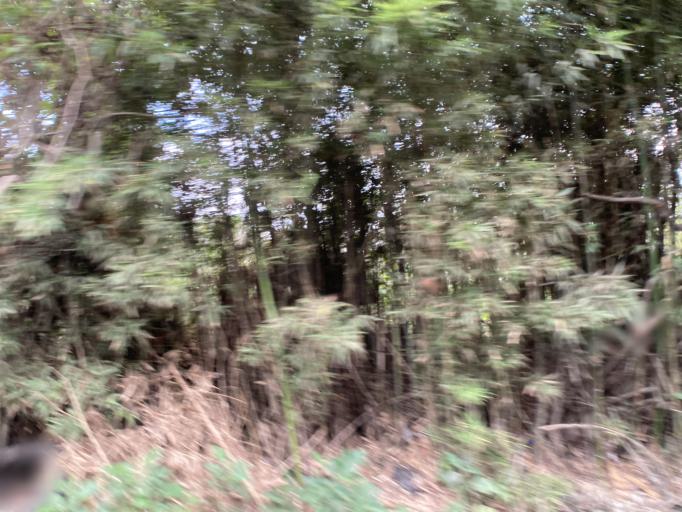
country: GT
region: Guatemala
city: Villa Canales
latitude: 14.4220
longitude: -90.5256
